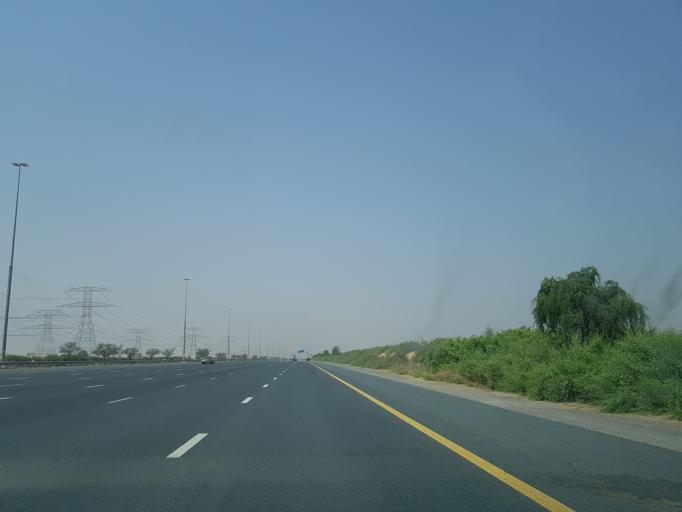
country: AE
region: Ash Shariqah
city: Sharjah
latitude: 25.1080
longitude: 55.4217
